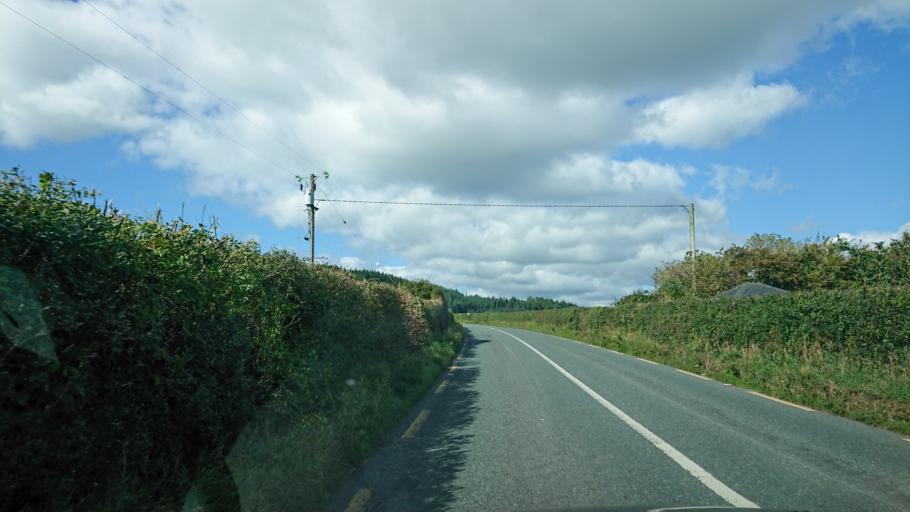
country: IE
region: Munster
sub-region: Waterford
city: Dungarvan
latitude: 52.1168
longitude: -7.6828
